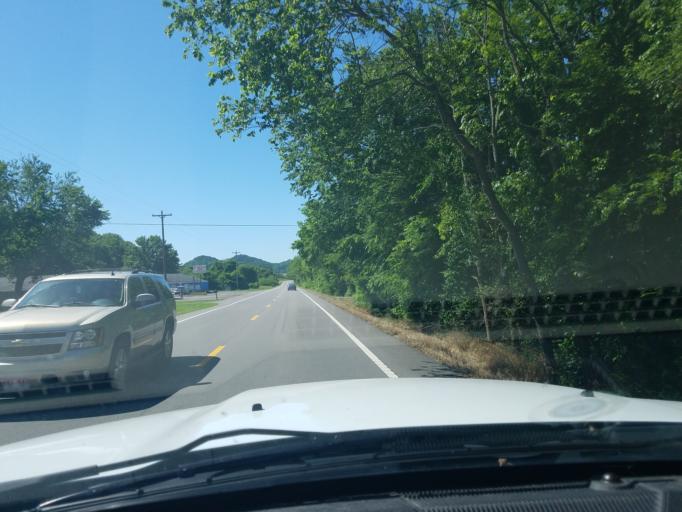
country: US
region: Tennessee
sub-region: Sumner County
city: Westmoreland
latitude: 36.4627
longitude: -86.2691
